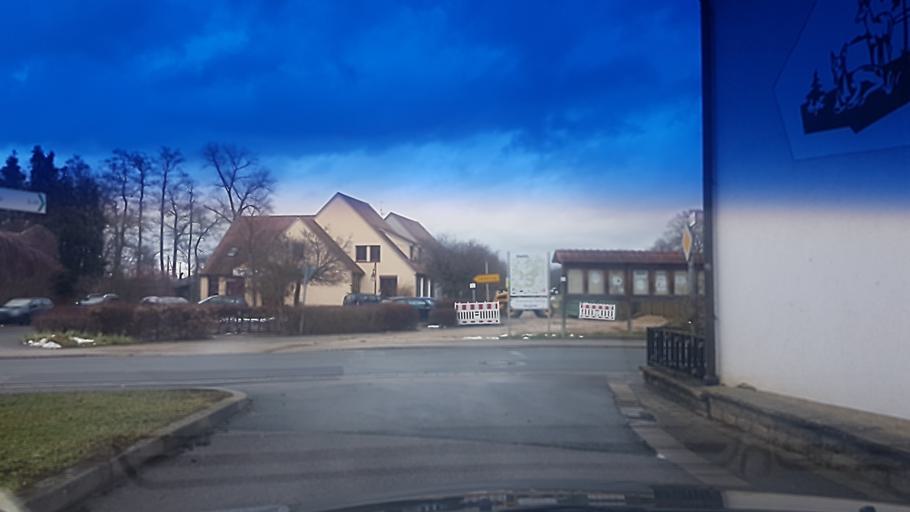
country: DE
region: Bavaria
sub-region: Upper Franconia
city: Schesslitz
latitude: 49.9608
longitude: 10.9971
